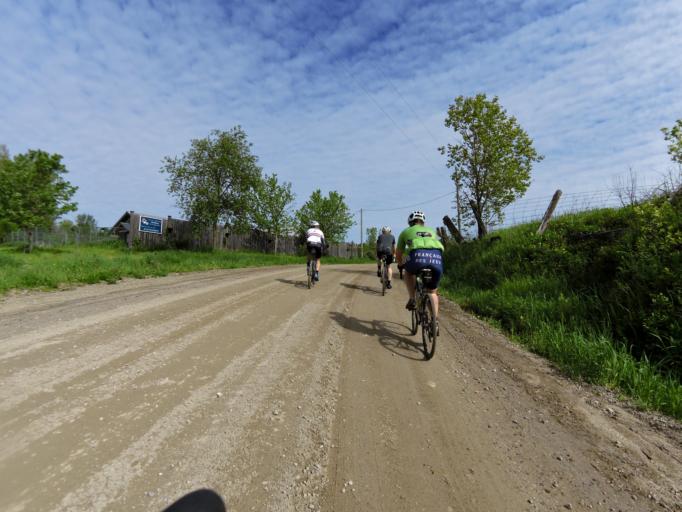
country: CA
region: Quebec
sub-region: Outaouais
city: Wakefield
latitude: 45.6982
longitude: -75.8953
